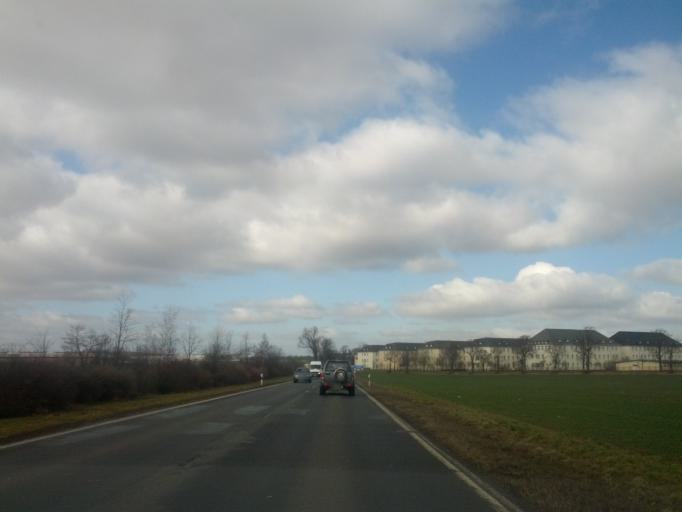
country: DE
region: Thuringia
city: Emleben
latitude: 50.9225
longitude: 10.7222
